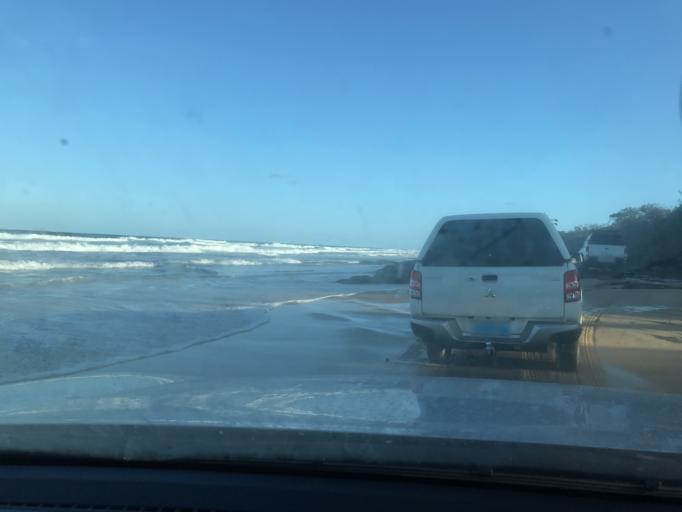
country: AU
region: Queensland
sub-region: Fraser Coast
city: Urangan
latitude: -25.4175
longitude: 153.1682
